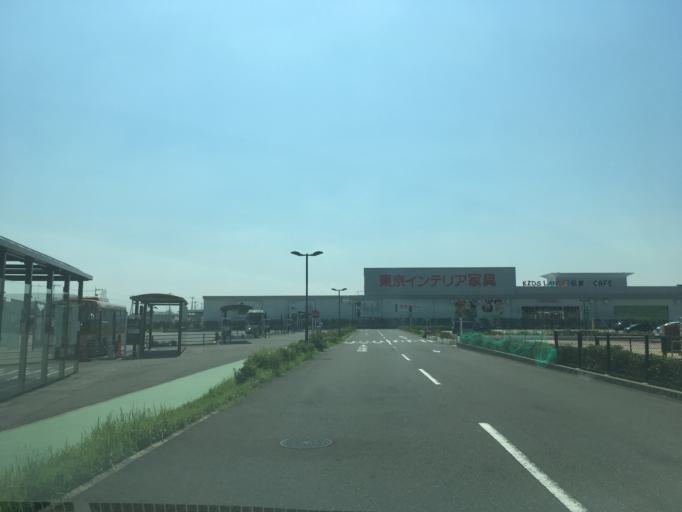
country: JP
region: Chiba
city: Kisarazu
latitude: 35.4346
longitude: 139.9378
